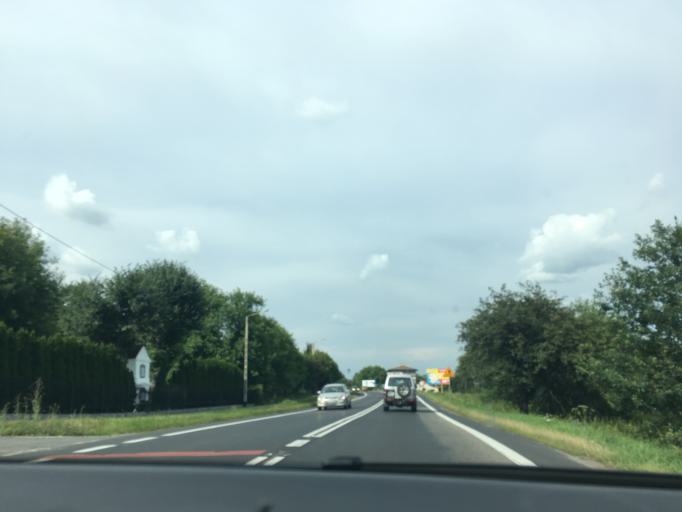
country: PL
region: Subcarpathian Voivodeship
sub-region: Powiat rzeszowski
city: Lubenia
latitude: 49.9374
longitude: 21.9049
